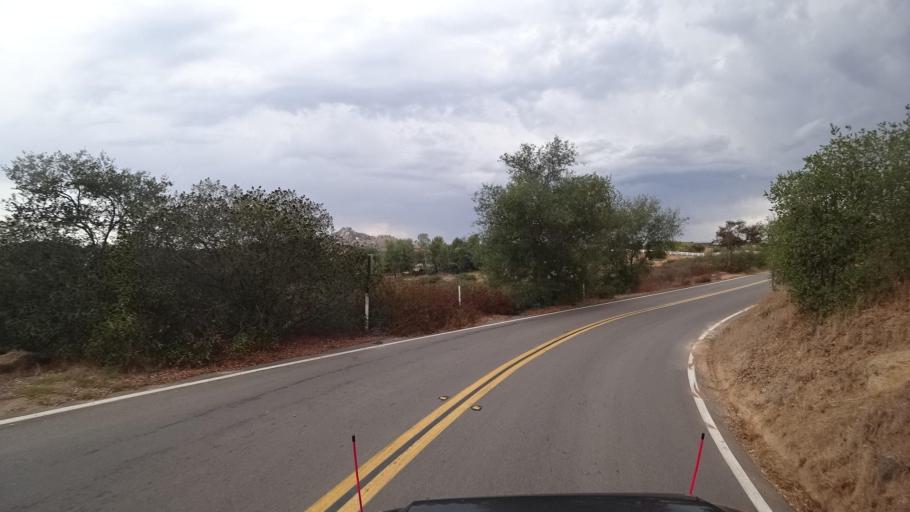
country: US
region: California
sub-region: San Diego County
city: San Pasqual
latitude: 33.0402
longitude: -116.9725
